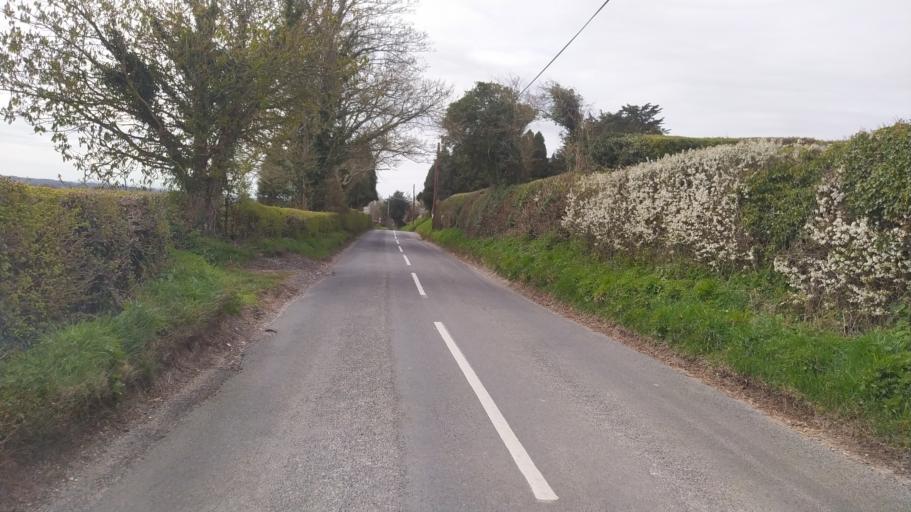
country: GB
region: England
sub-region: Hampshire
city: Bishops Waltham
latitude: 50.9712
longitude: -1.2074
